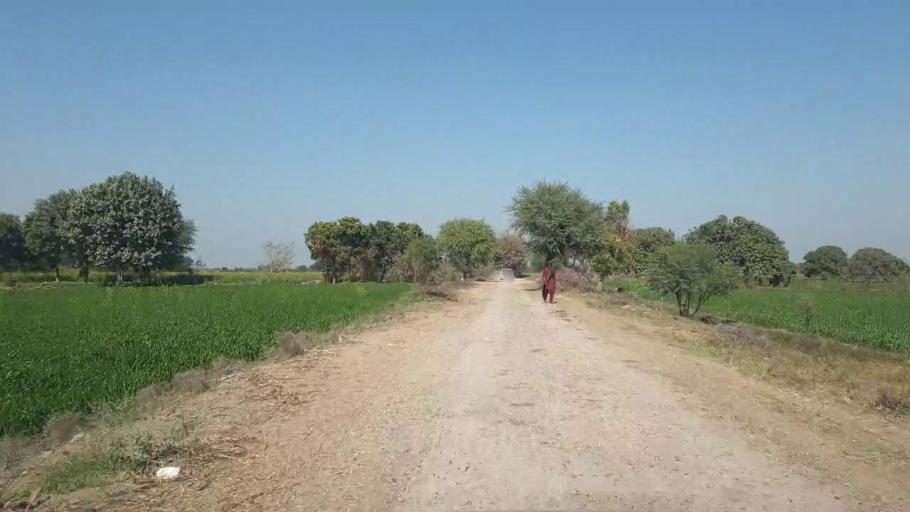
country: PK
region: Sindh
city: Chambar
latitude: 25.2994
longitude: 68.6918
